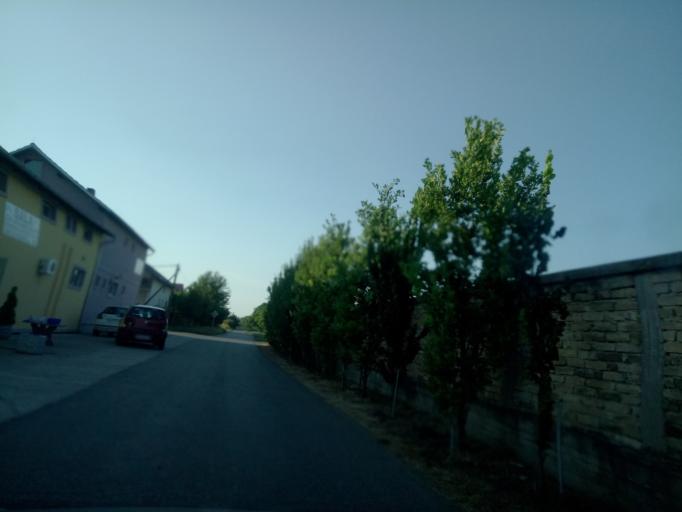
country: RS
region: Autonomna Pokrajina Vojvodina
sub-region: Sremski Okrug
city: Stara Pazova
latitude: 44.9940
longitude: 20.1623
